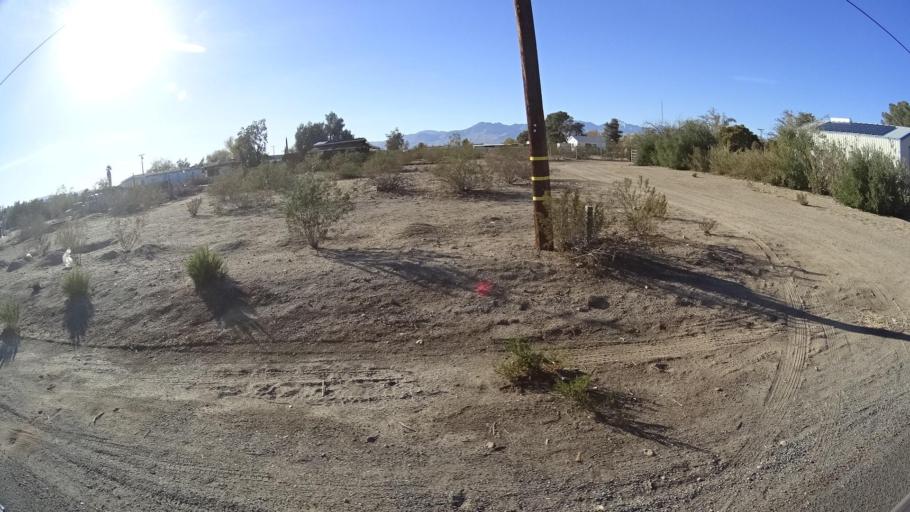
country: US
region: California
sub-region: Kern County
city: Ridgecrest
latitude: 35.6435
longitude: -117.7056
